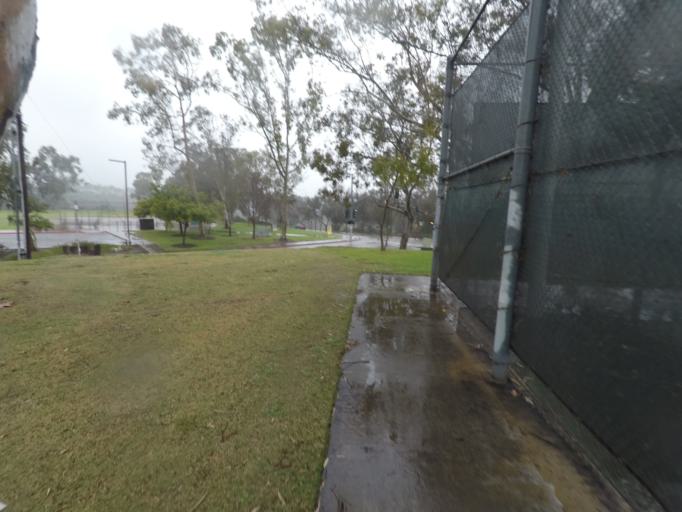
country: US
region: California
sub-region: San Diego County
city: San Diego
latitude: 32.7933
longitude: -117.1705
